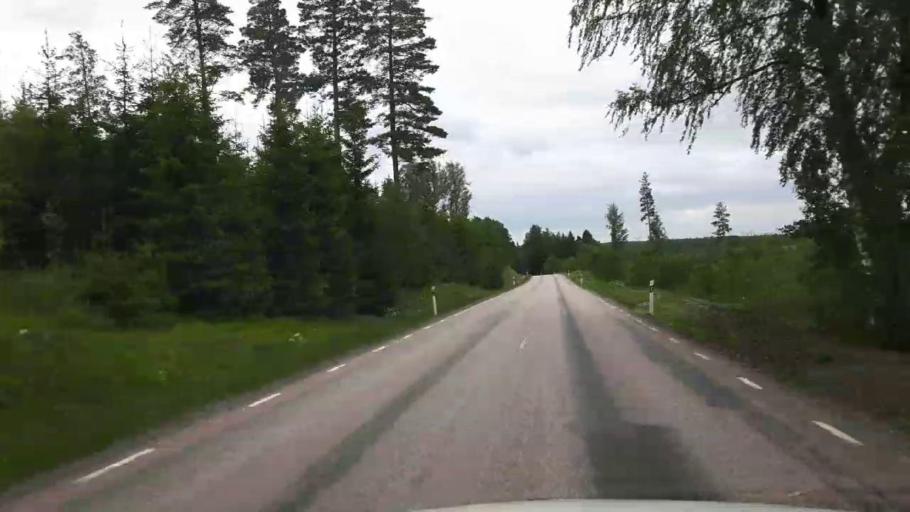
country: SE
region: Vaestmanland
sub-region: Kopings Kommun
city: Kolsva
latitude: 59.6385
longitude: 15.7962
